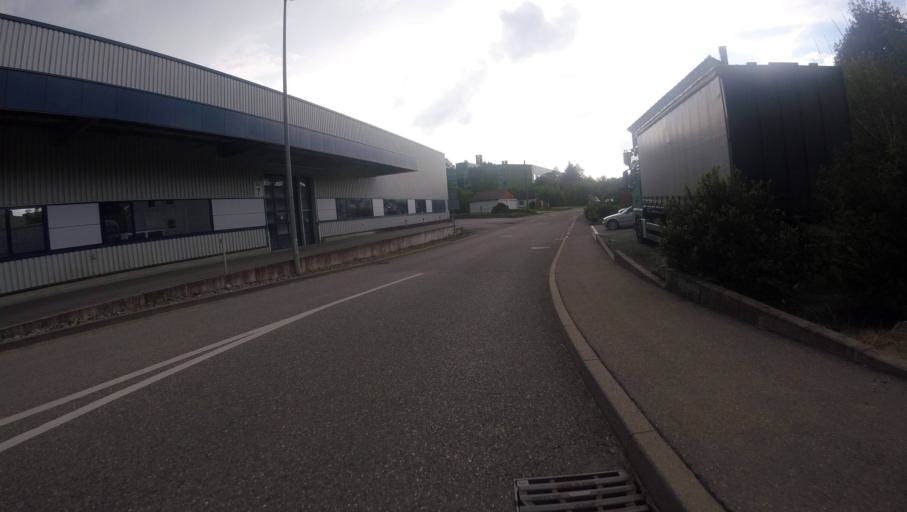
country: DE
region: Baden-Wuerttemberg
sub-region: Regierungsbezirk Stuttgart
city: Sulzbach an der Murr
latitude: 49.0008
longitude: 9.5110
